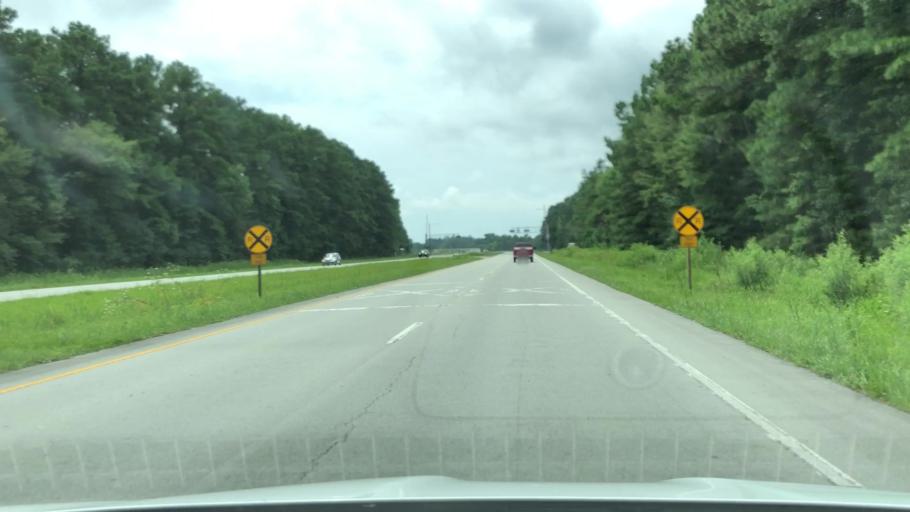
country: US
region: North Carolina
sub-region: Carteret County
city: Newport
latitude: 34.8179
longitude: -76.8782
